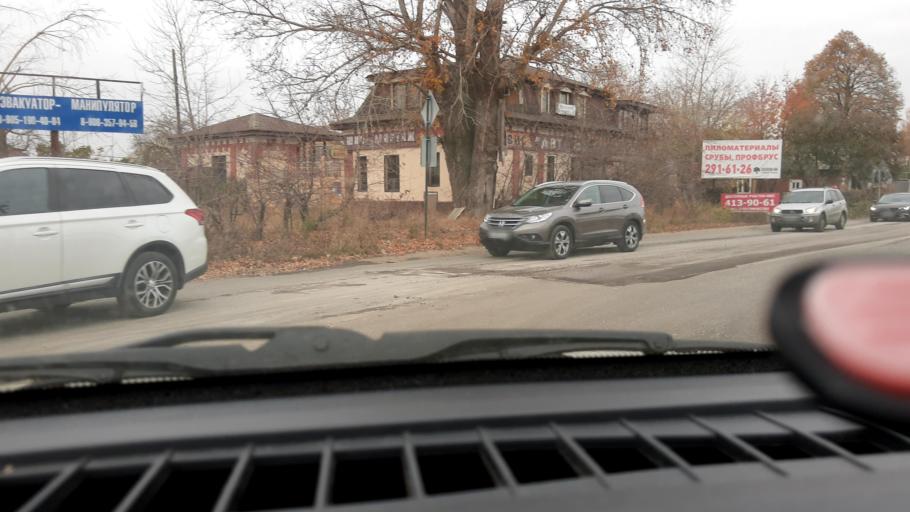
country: RU
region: Nizjnij Novgorod
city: Neklyudovo
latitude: 56.3994
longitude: 43.9813
